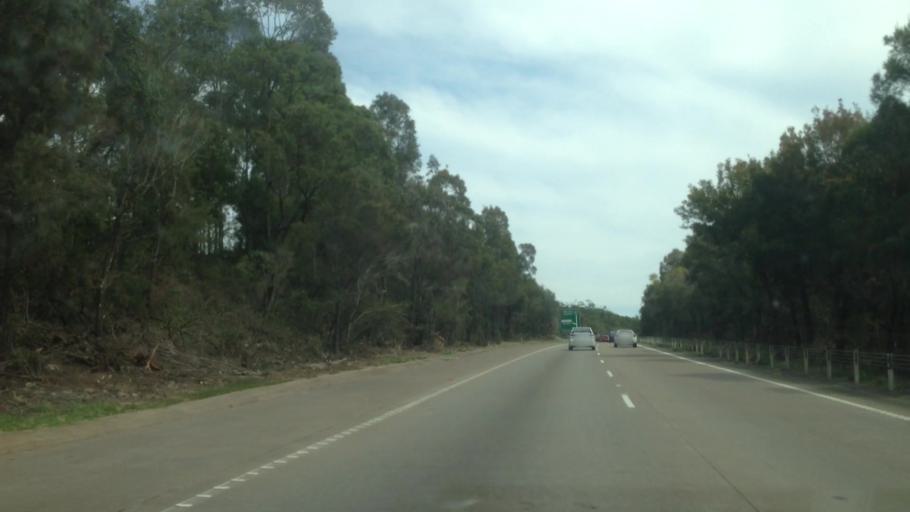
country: AU
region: New South Wales
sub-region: Lake Macquarie Shire
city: Fennell Bay
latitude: -32.9743
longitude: 151.5320
